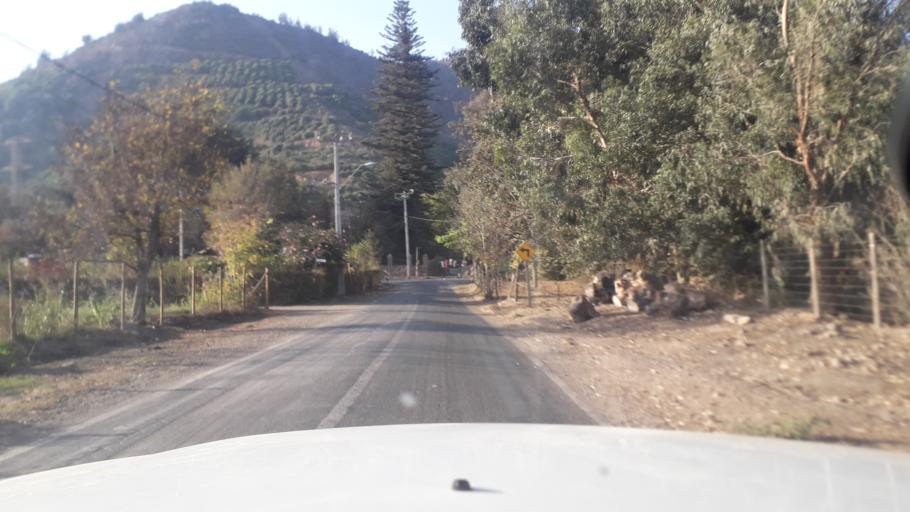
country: CL
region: Valparaiso
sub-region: Provincia de San Felipe
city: Llaillay
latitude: -32.8205
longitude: -71.0274
